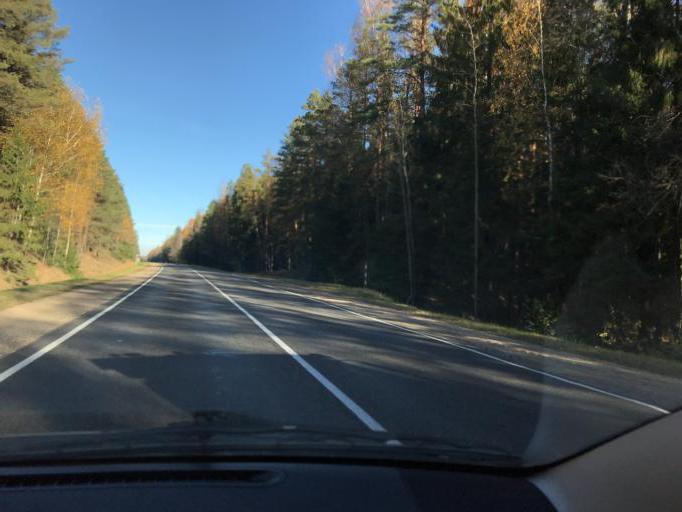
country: BY
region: Vitebsk
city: Polatsk
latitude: 55.3606
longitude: 28.8067
